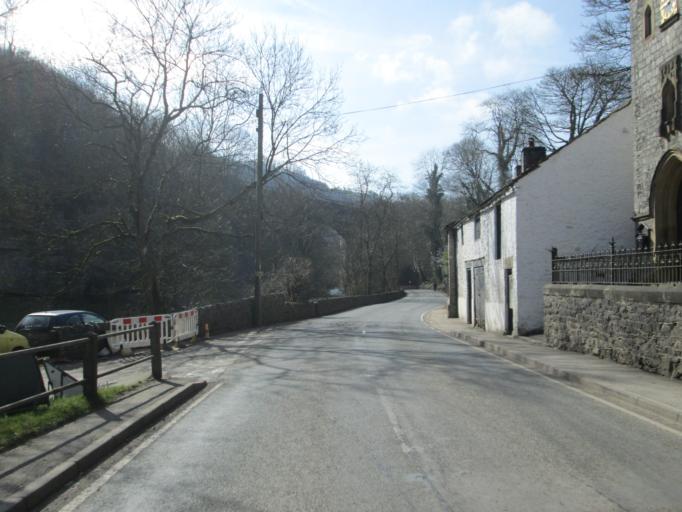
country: GB
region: England
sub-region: Derbyshire
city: Tideswell
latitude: 53.2567
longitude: -1.7894
